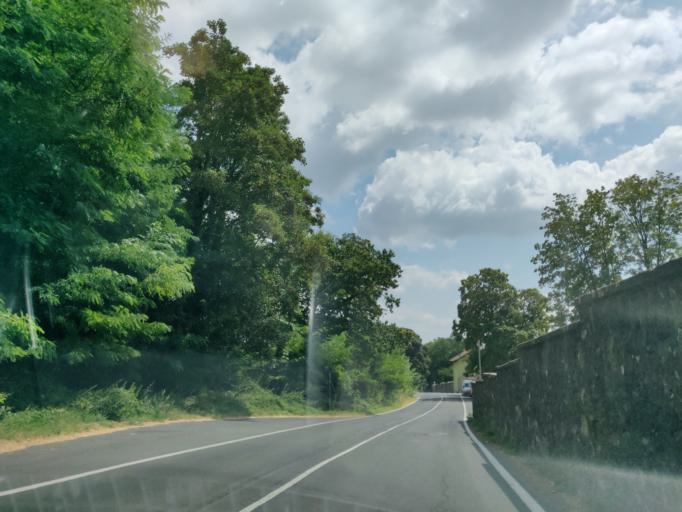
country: IT
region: Tuscany
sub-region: Provincia di Siena
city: Abbadia San Salvatore
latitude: 42.8836
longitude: 11.6638
